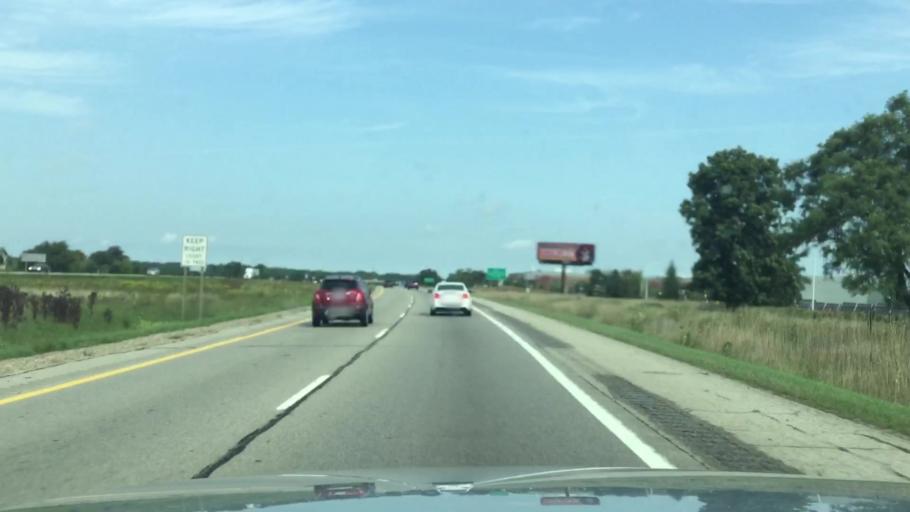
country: US
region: Michigan
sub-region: Kalamazoo County
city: Westwood
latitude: 42.2514
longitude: -85.6433
